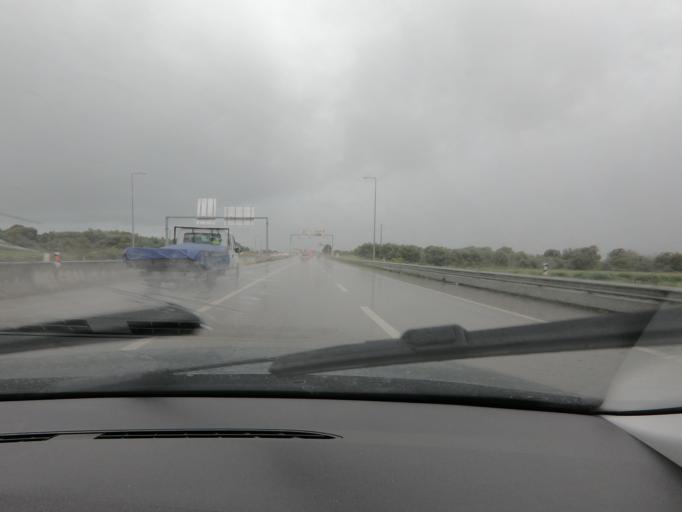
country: PT
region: Lisbon
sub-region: Sintra
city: Sintra
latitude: 38.8141
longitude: -9.3584
